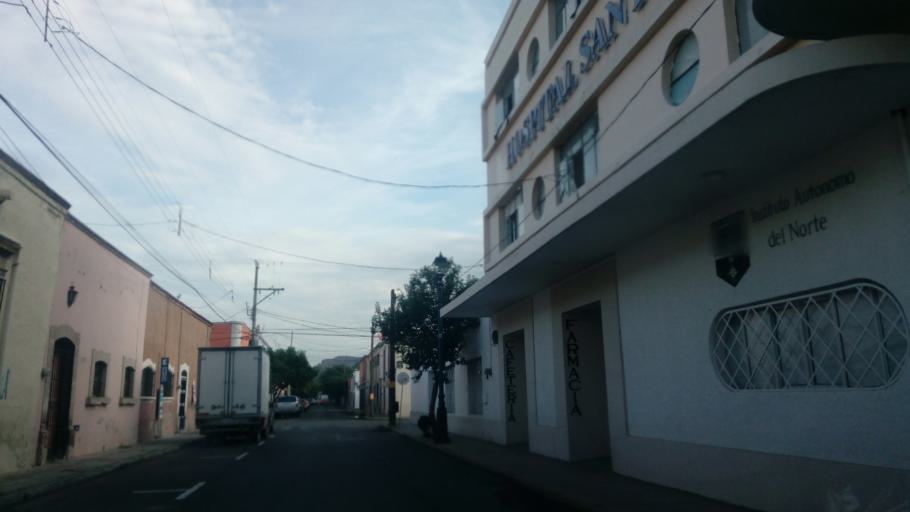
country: MX
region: Durango
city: Victoria de Durango
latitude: 24.0311
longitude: -104.6706
